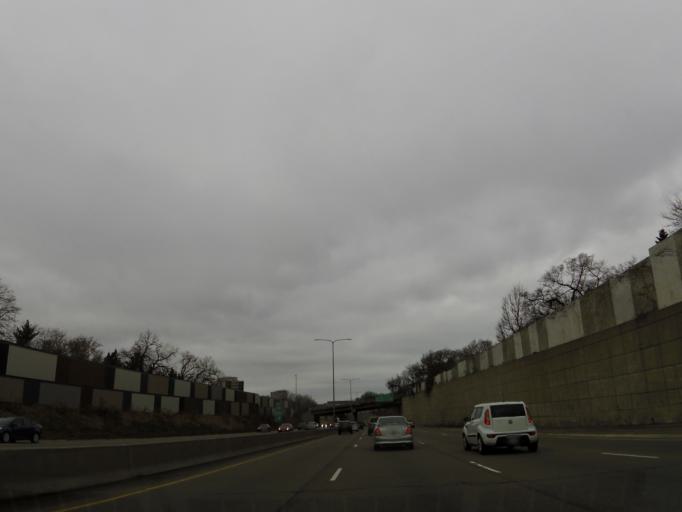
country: US
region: Minnesota
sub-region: Ramsey County
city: Lauderdale
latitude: 44.9631
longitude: -93.2140
